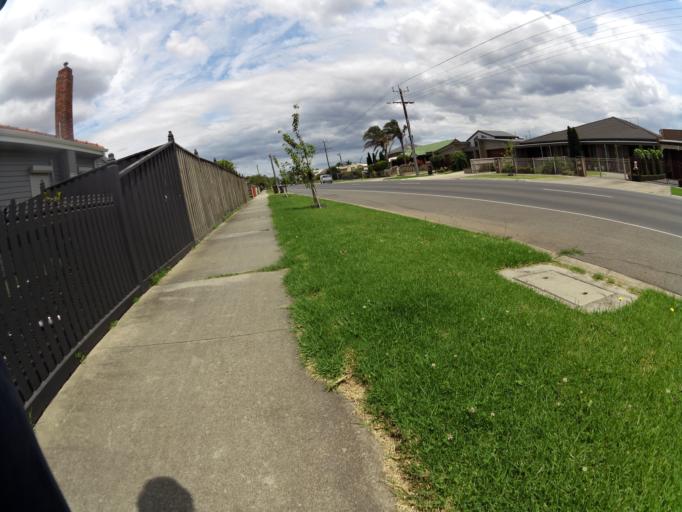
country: AU
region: Victoria
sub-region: Latrobe
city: Traralgon
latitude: -38.1900
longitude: 146.5342
